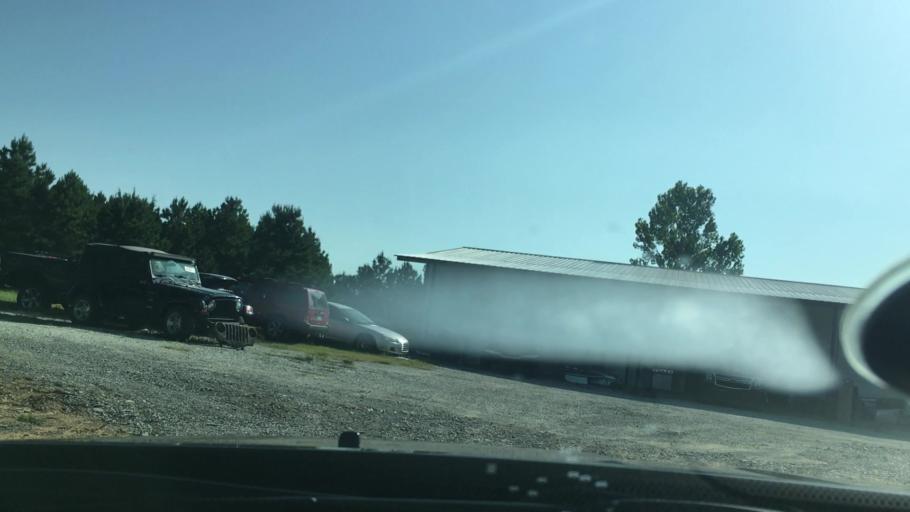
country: US
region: Oklahoma
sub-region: Pontotoc County
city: Byng
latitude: 34.8197
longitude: -96.6243
